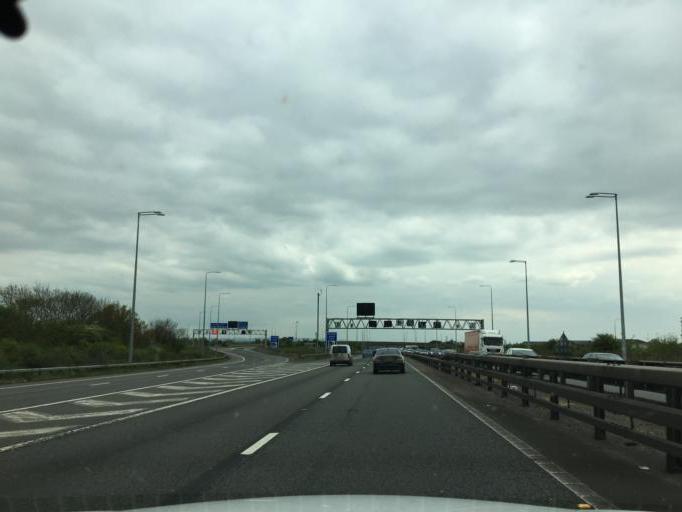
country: GB
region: England
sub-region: South Gloucestershire
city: Almondsbury
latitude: 51.5552
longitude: -2.5555
